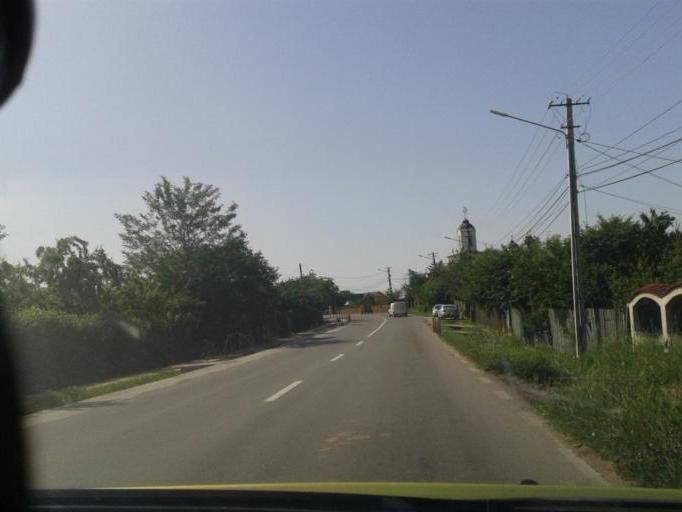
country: RO
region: Prahova
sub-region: Comuna Paulesti
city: Gageni
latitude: 45.0198
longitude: 25.9449
